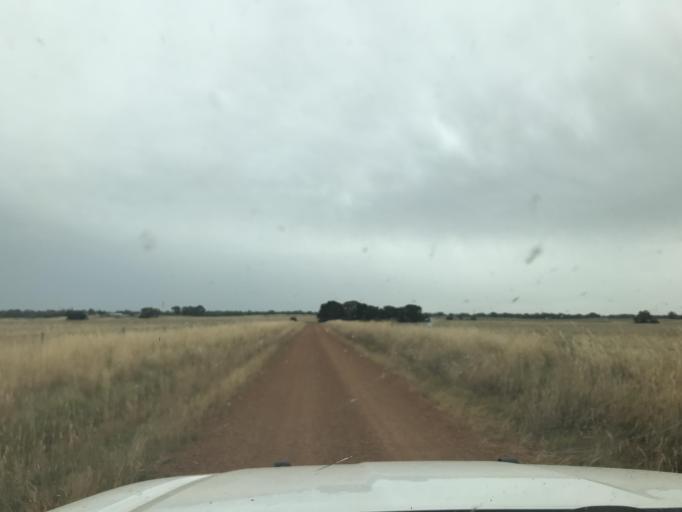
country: AU
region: Victoria
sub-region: Horsham
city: Horsham
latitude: -37.0598
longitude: 141.6033
